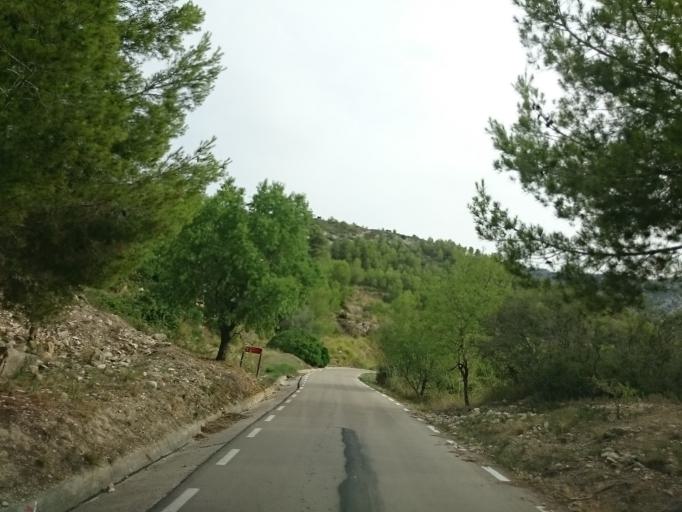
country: ES
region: Catalonia
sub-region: Provincia de Barcelona
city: Olivella
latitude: 41.3064
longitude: 1.8388
